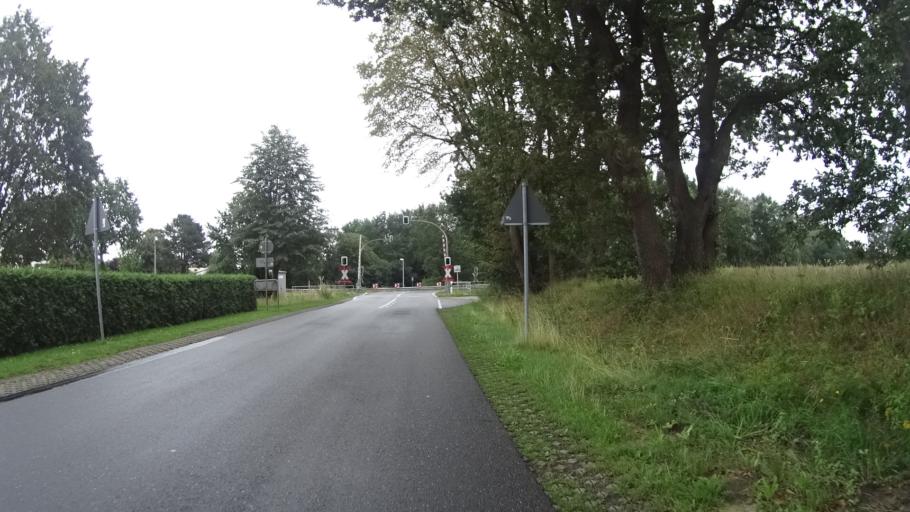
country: DE
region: Schleswig-Holstein
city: Henstedt-Ulzburg
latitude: 53.7715
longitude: 9.9711
